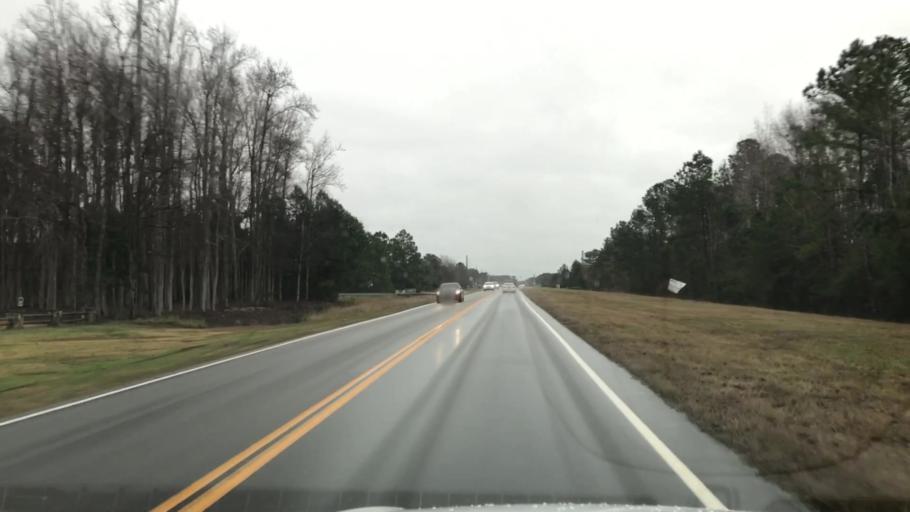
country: US
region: South Carolina
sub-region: Horry County
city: Myrtle Beach
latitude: 33.7343
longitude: -78.9020
